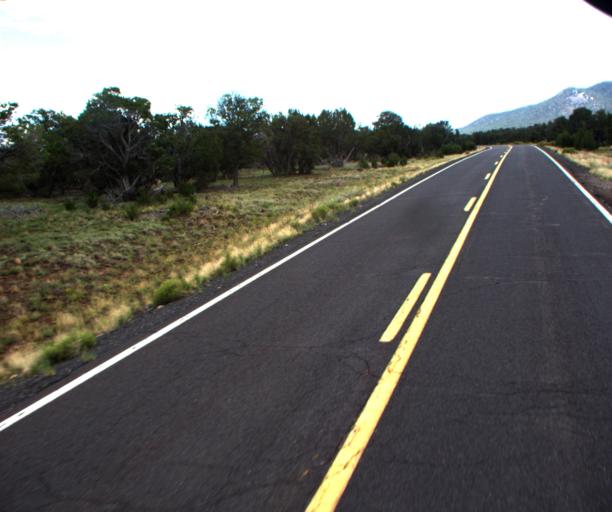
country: US
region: Arizona
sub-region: Coconino County
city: Parks
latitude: 35.5355
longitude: -111.8517
